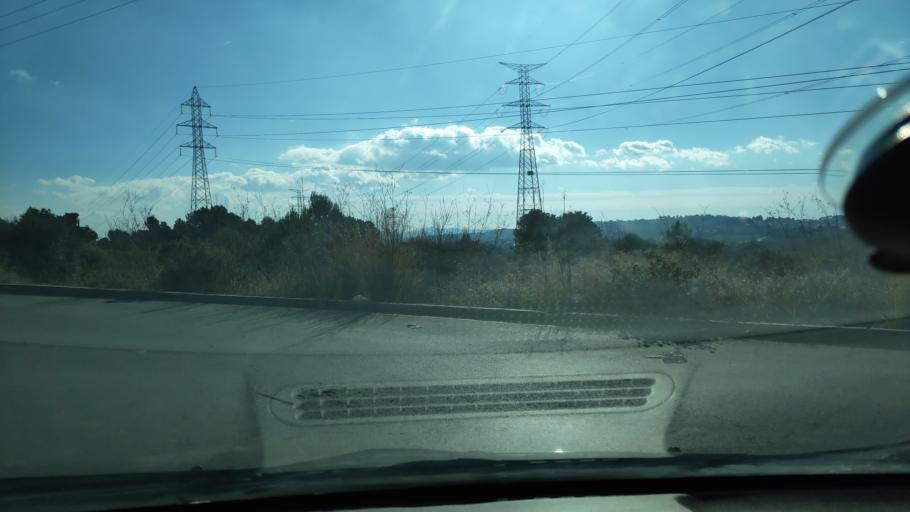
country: ES
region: Catalonia
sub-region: Provincia de Barcelona
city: Terrassa
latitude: 41.5561
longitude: 2.0516
